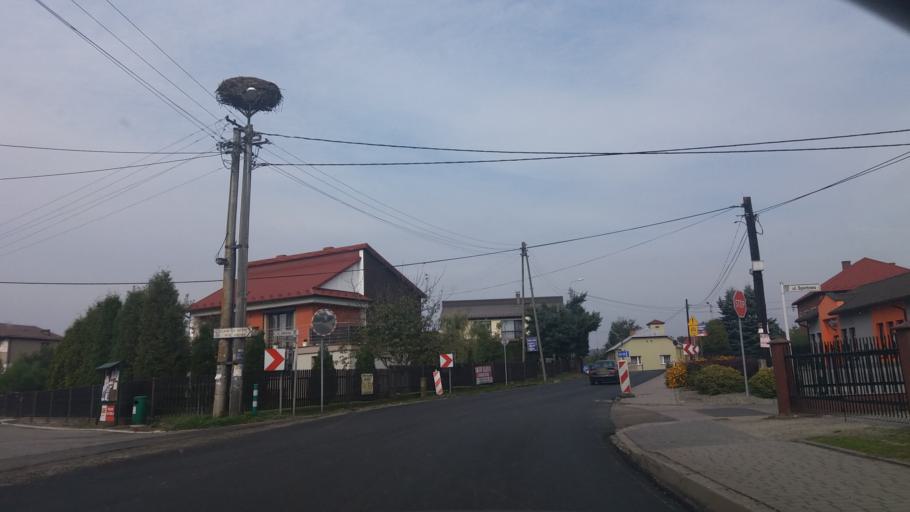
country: PL
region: Lesser Poland Voivodeship
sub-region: Powiat chrzanowski
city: Babice
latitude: 50.0406
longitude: 19.4407
